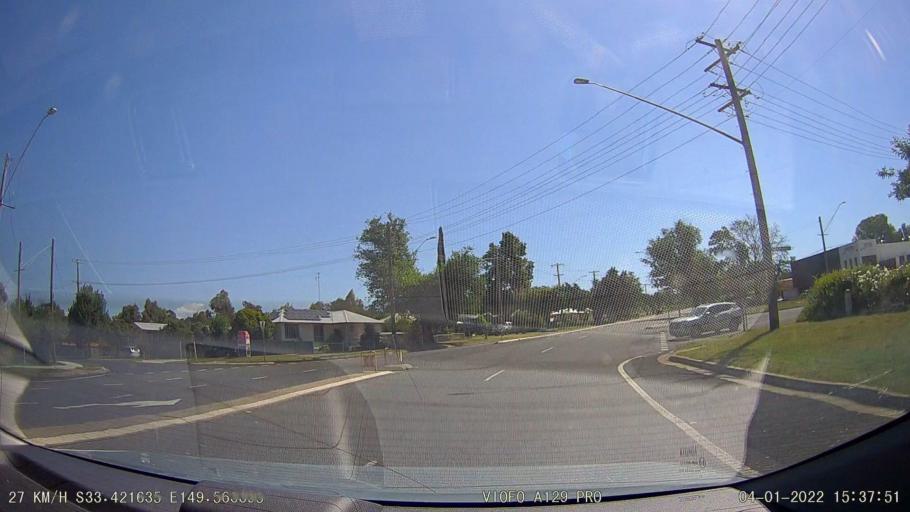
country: AU
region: New South Wales
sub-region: Bathurst Regional
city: Bathurst
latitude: -33.4215
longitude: 149.5636
